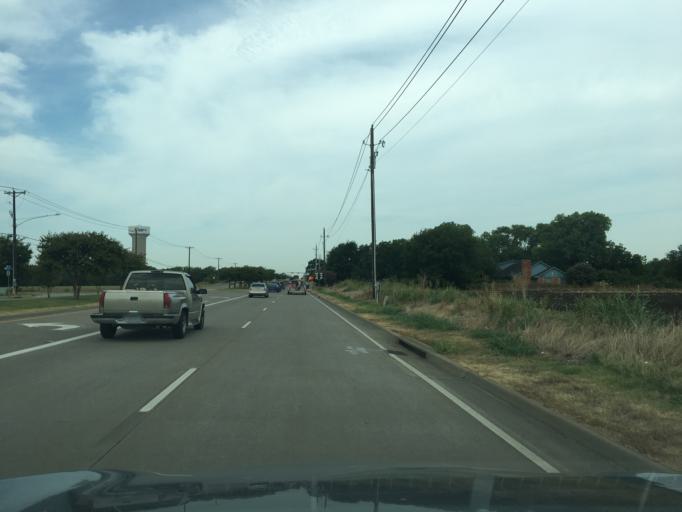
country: US
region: Texas
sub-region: Collin County
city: Parker
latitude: 33.0554
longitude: -96.6151
